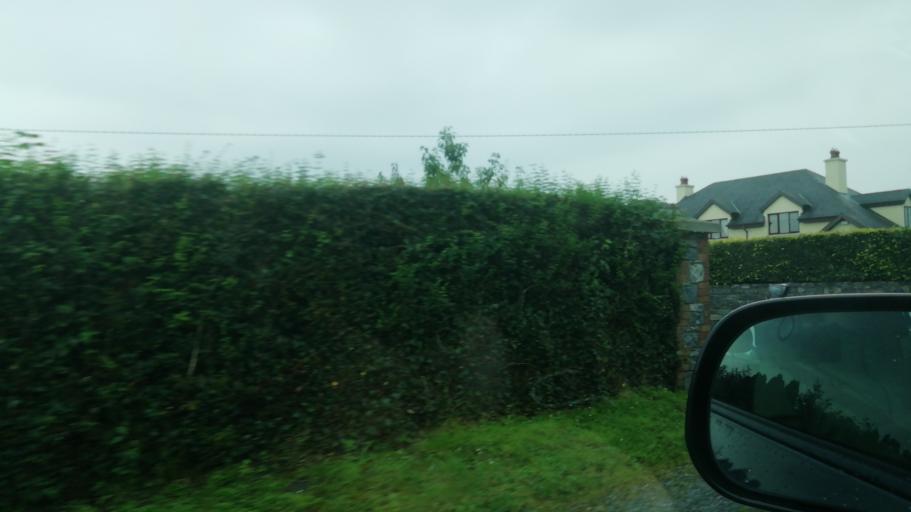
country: IE
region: Leinster
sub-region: Kilkenny
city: Thomastown
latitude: 52.6117
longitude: -7.1059
